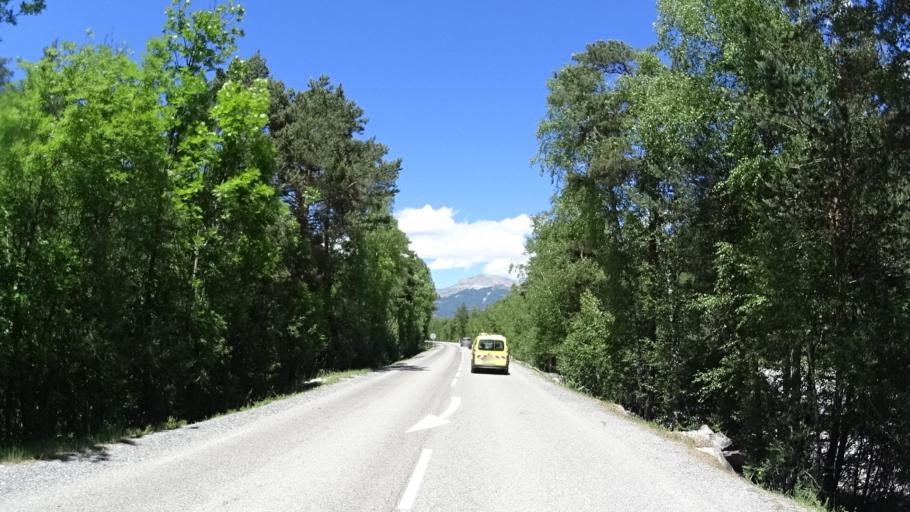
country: FR
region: Provence-Alpes-Cote d'Azur
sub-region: Departement des Alpes-de-Haute-Provence
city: Annot
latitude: 44.1458
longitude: 6.5961
